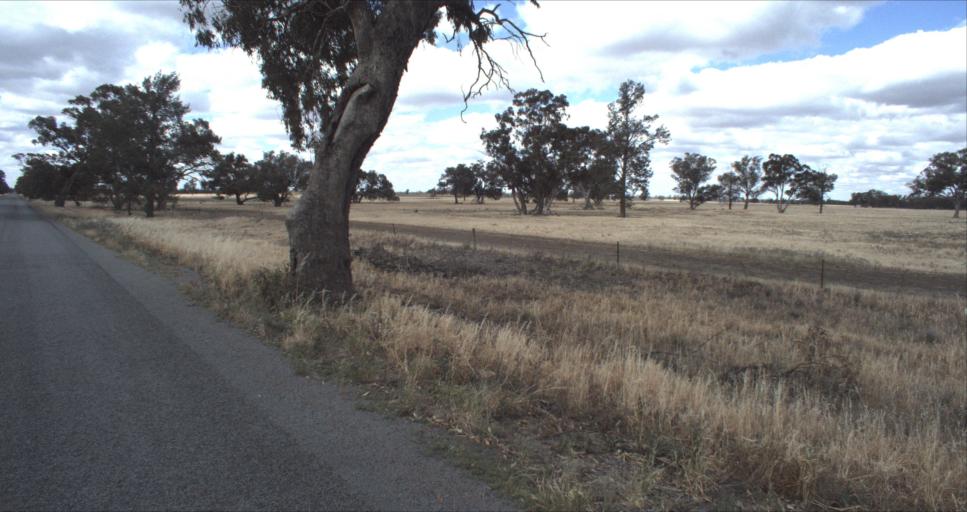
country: AU
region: New South Wales
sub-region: Leeton
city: Leeton
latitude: -34.6879
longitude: 146.3443
